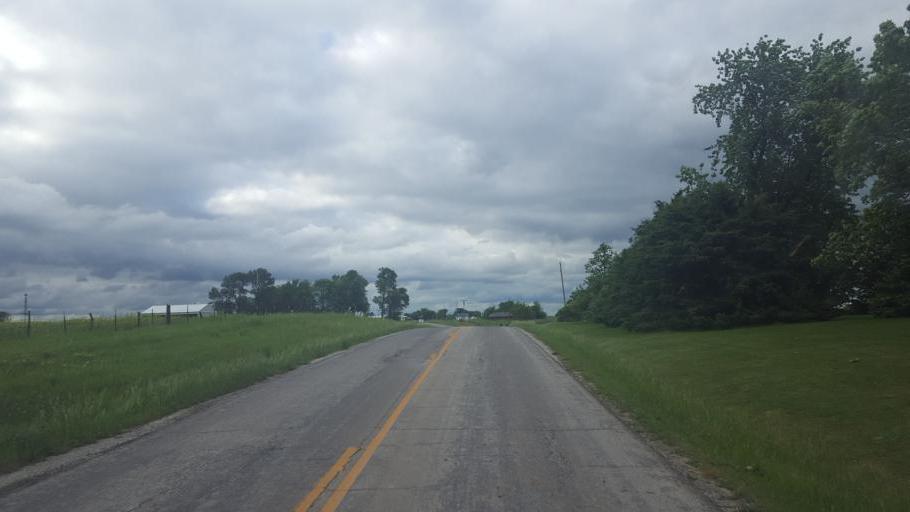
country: US
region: Missouri
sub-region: Mercer County
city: Princeton
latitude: 40.2910
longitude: -93.6802
